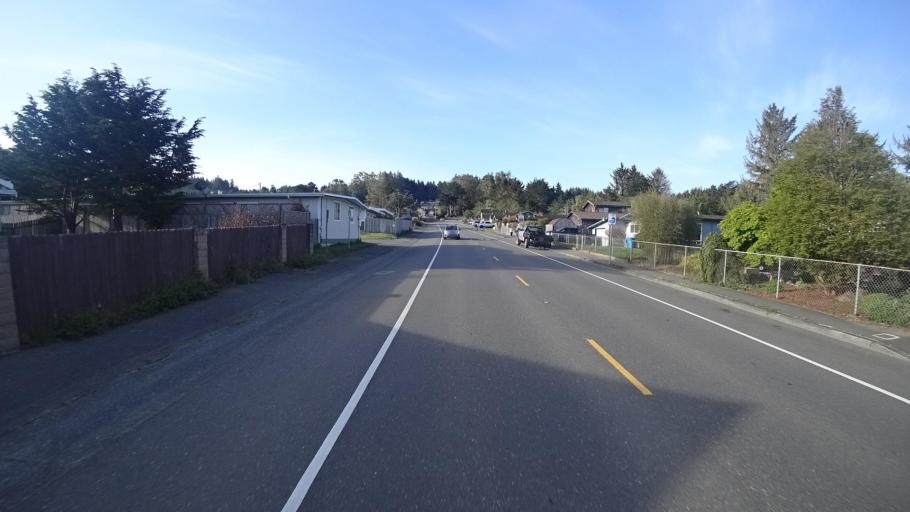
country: US
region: California
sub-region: Humboldt County
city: Humboldt Hill
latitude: 40.7321
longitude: -124.2022
